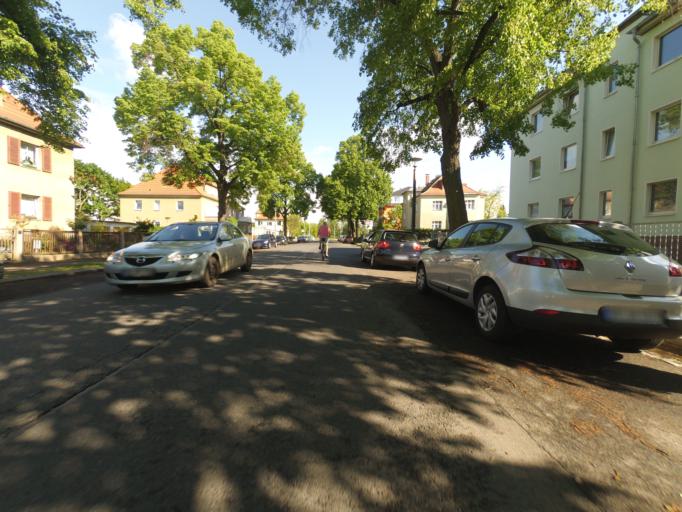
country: DE
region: Saxony
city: Heidenau
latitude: 51.0161
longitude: 13.8126
